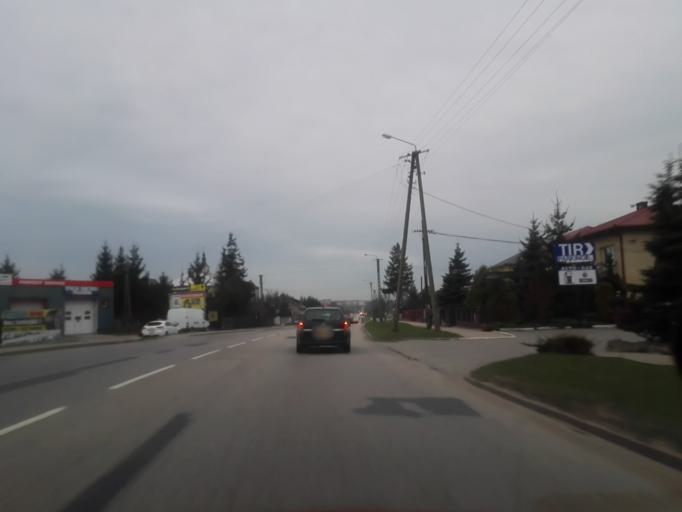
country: PL
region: Podlasie
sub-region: Powiat lomzynski
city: Piatnica
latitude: 53.1988
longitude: 22.0991
